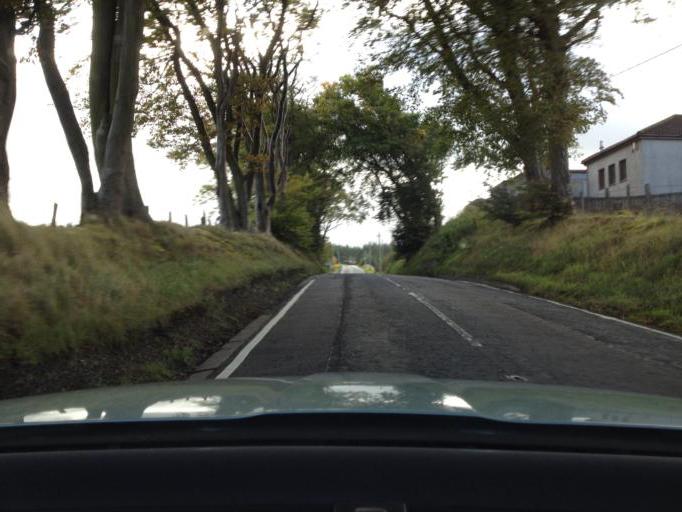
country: GB
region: Scotland
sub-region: West Lothian
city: West Calder
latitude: 55.8379
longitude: -3.5371
